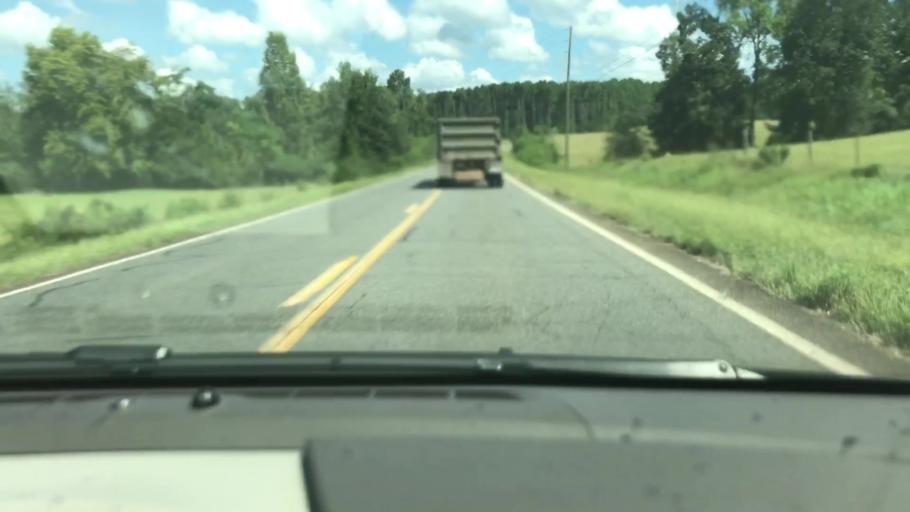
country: US
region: Alabama
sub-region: Chambers County
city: Valley
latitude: 32.8337
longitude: -85.0356
